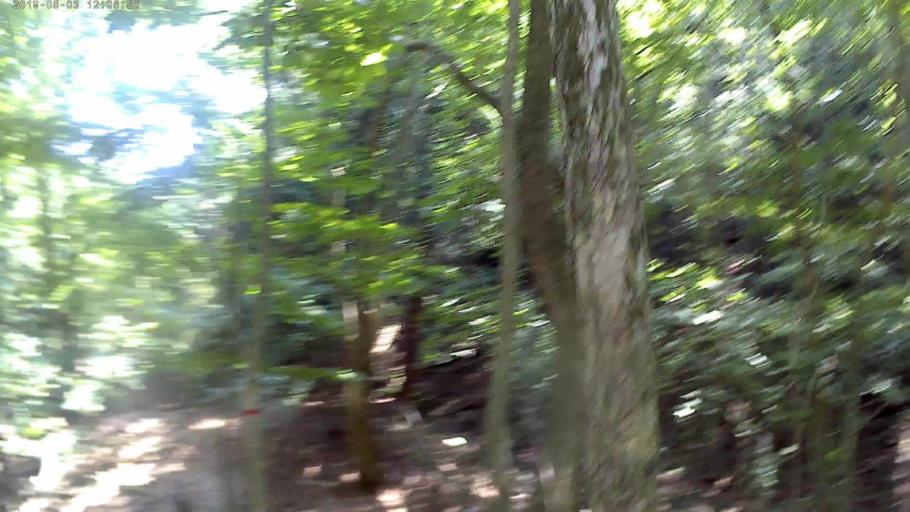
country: JP
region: Yamanashi
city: Enzan
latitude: 35.6121
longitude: 138.7856
